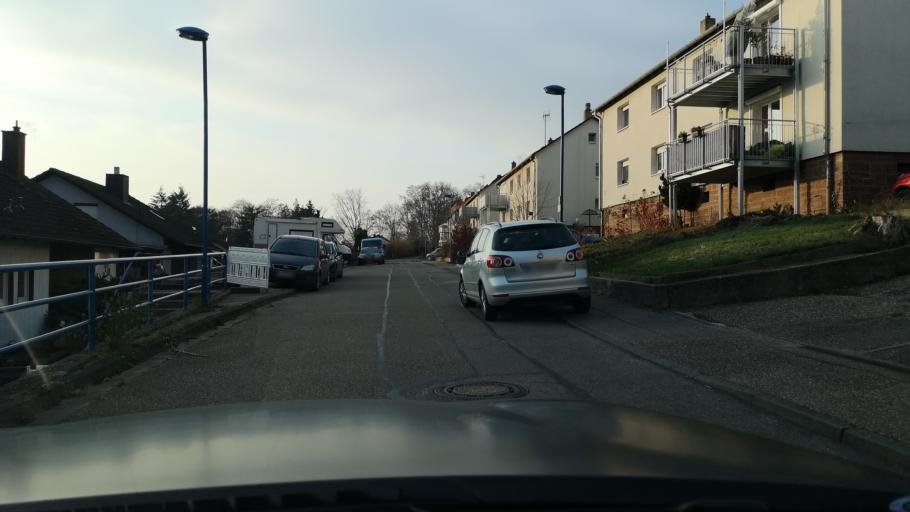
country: DE
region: Baden-Wuerttemberg
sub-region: Karlsruhe Region
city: Ettlingen
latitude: 48.9315
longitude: 8.4554
